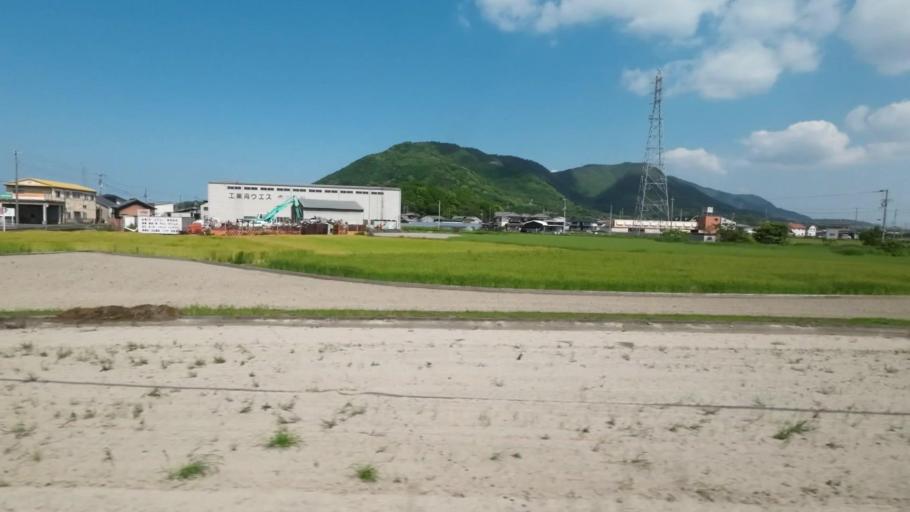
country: JP
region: Kagawa
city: Kan'onjicho
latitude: 34.1330
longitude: 133.6823
